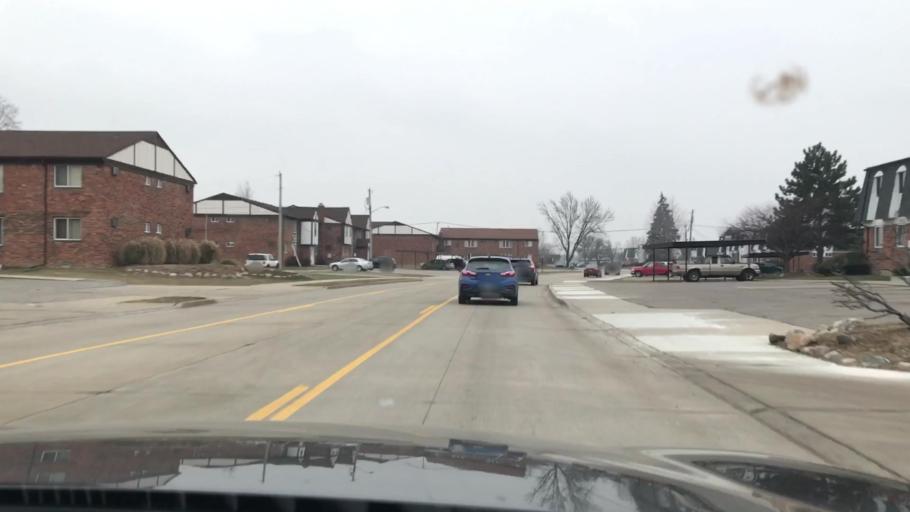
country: US
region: Michigan
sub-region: Oakland County
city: Clawson
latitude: 42.5308
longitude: -83.1131
